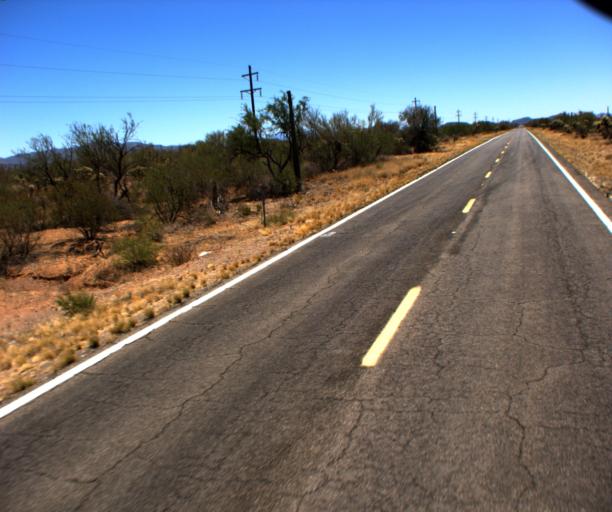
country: US
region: Arizona
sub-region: Pima County
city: Sells
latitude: 32.0517
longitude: -112.0267
